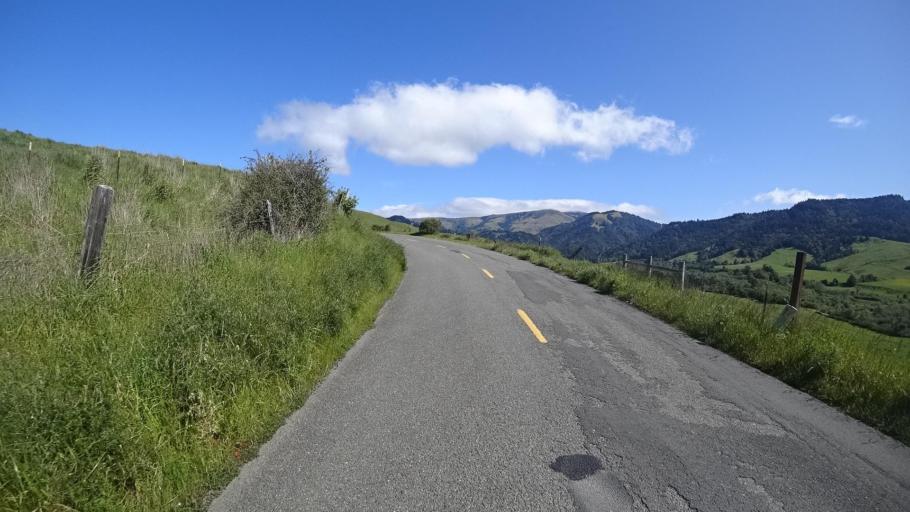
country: US
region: California
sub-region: Humboldt County
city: Ferndale
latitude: 40.3327
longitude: -124.2984
